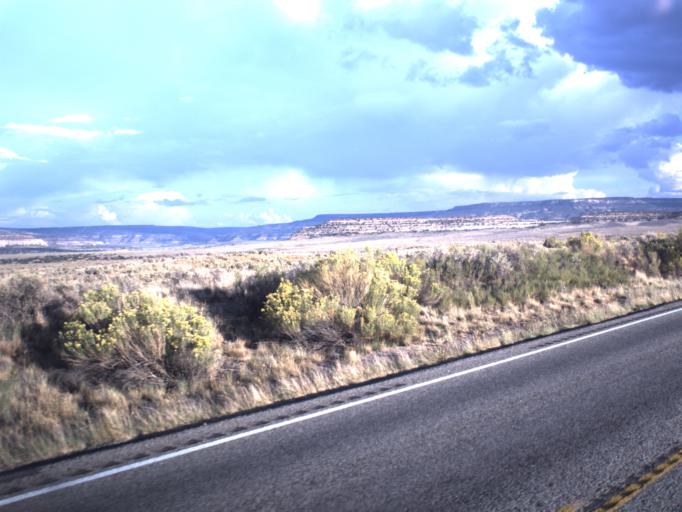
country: US
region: Utah
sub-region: San Juan County
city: Monticello
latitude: 38.1350
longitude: -109.3702
